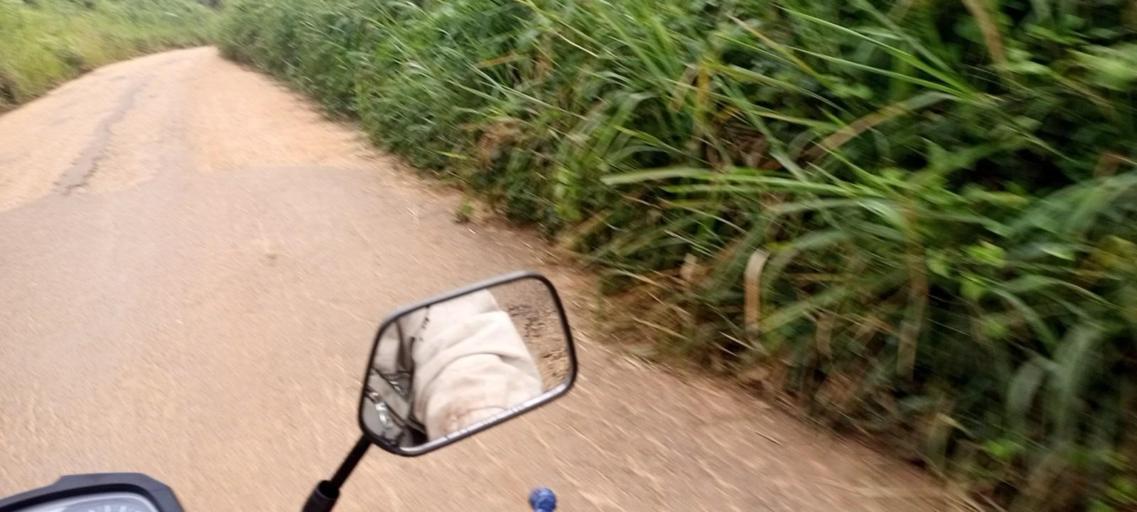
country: CD
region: Eastern Province
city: Kisangani
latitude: 0.1859
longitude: 25.5270
